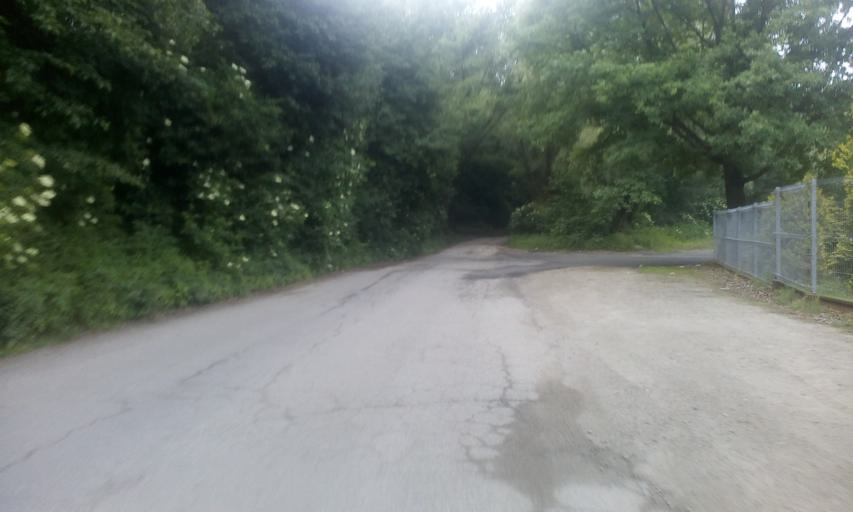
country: PL
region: Lesser Poland Voivodeship
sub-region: Powiat nowosadecki
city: Stary Sacz
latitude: 49.5828
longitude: 20.6616
